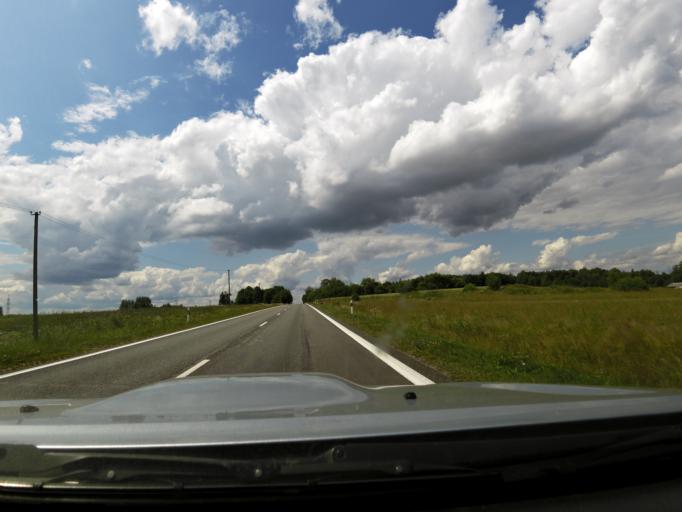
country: LT
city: Jieznas
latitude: 54.5814
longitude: 24.2161
